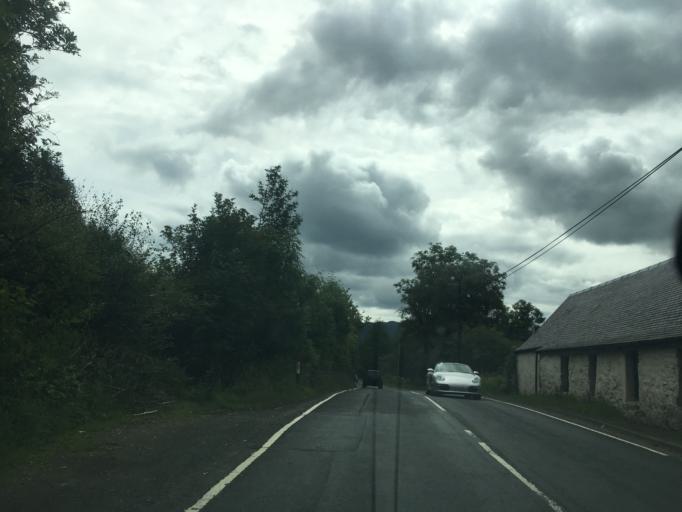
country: GB
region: Scotland
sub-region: Stirling
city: Callander
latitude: 56.3413
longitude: -4.3260
